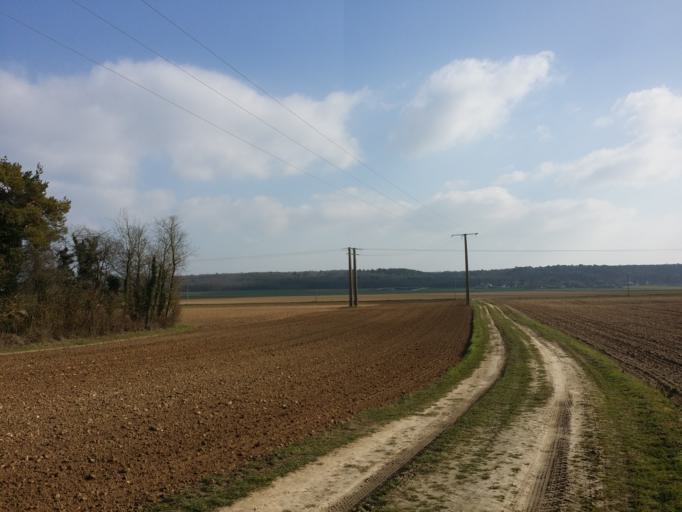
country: FR
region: Ile-de-France
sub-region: Departement de Seine-et-Marne
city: Montcourt-Fromonville
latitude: 48.2852
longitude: 2.7375
